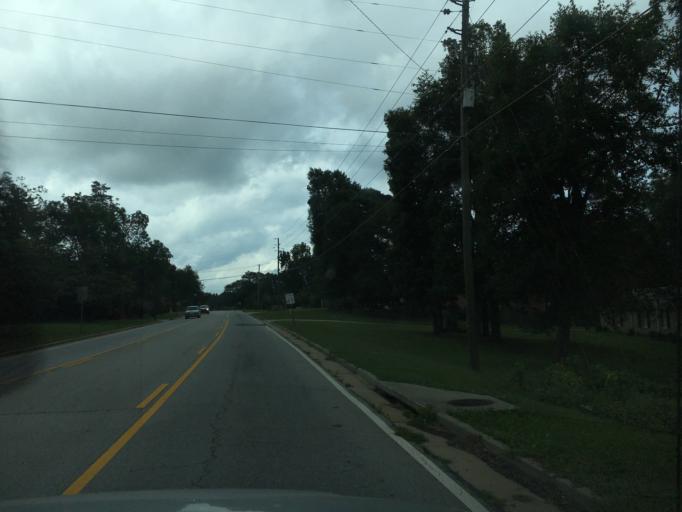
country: US
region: Georgia
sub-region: Rockdale County
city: Conyers
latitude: 33.6565
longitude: -84.0500
